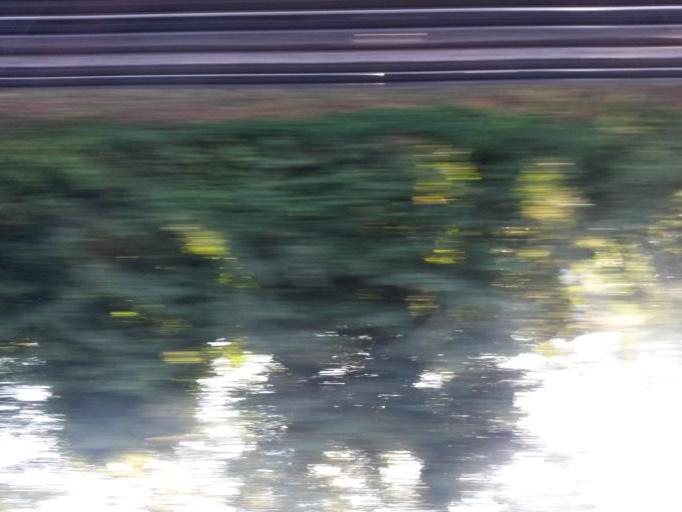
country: GB
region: England
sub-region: Greater London
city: Brixton Hill
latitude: 51.4282
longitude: -0.1385
